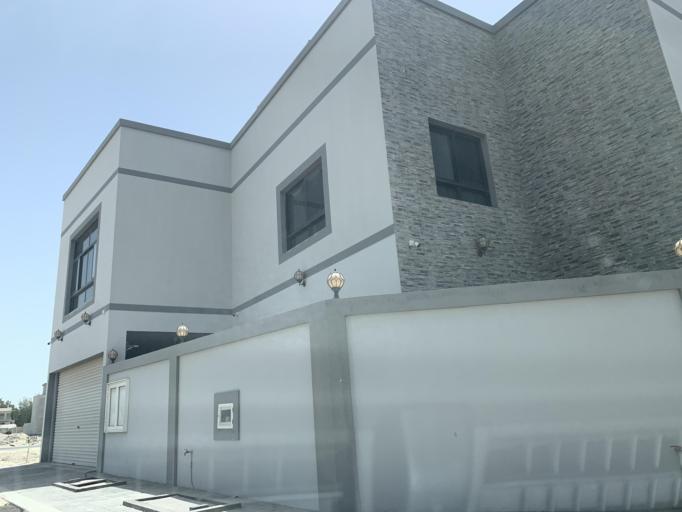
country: BH
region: Northern
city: Madinat `Isa
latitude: 26.1611
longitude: 50.5786
